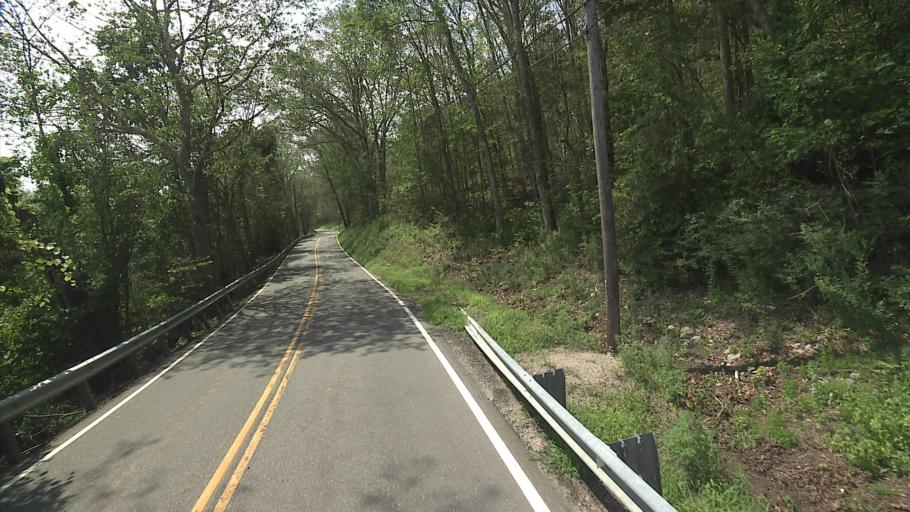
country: US
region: Connecticut
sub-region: Windham County
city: Moosup
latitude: 41.7547
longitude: -71.8533
